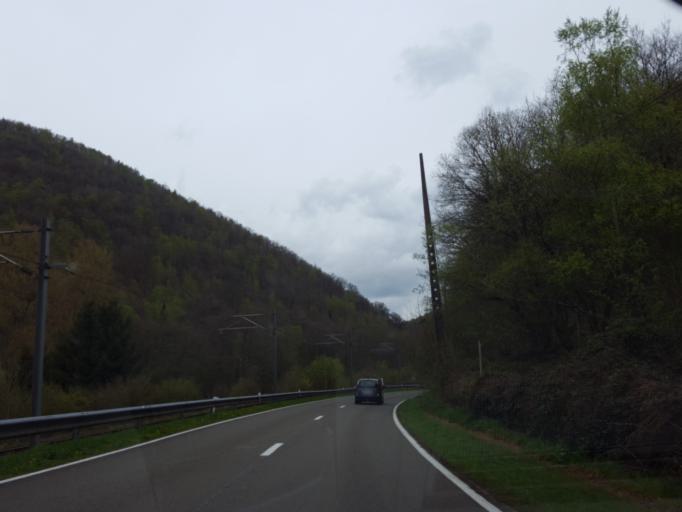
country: BE
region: Wallonia
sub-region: Province de Liege
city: Aywaille
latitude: 50.4487
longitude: 5.7384
